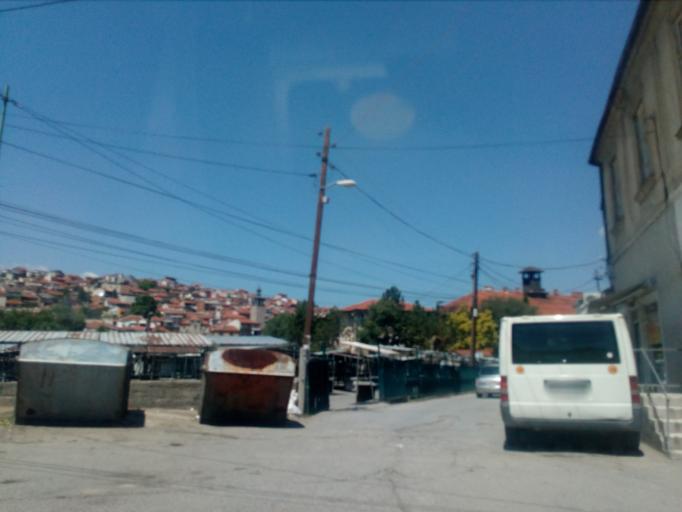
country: MK
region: Veles
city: Veles
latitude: 41.7128
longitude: 21.7872
